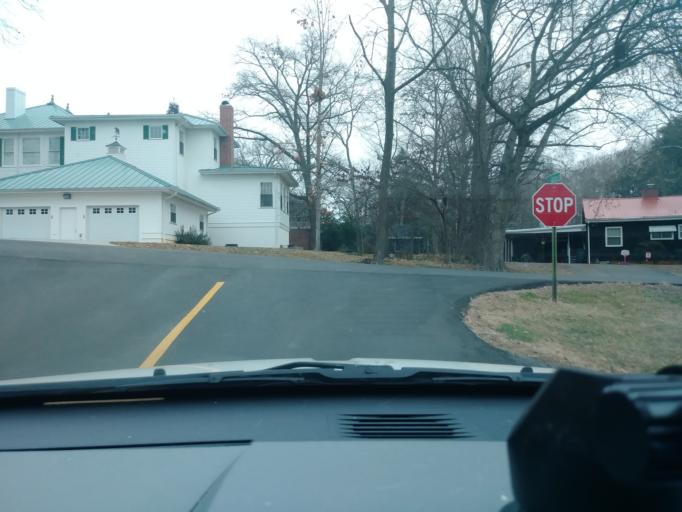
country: US
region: Tennessee
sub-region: Greene County
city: Greeneville
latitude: 36.1580
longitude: -82.8378
